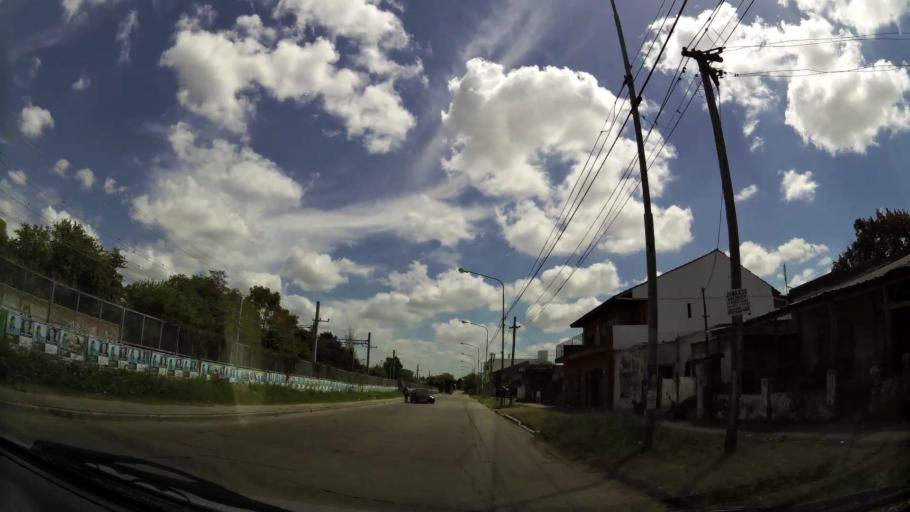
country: AR
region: Buenos Aires
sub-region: Partido de Quilmes
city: Quilmes
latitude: -34.8106
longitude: -58.2634
